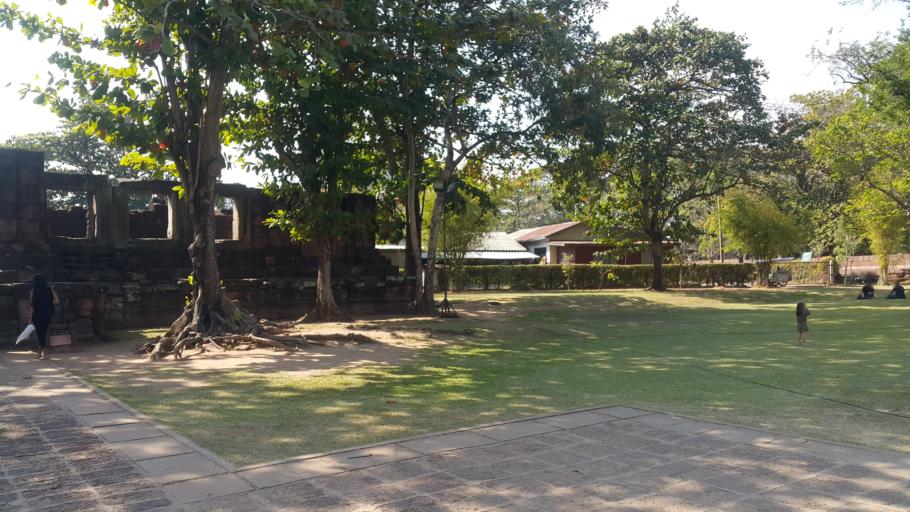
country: TH
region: Nakhon Ratchasima
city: Phimai
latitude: 15.2192
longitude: 102.4945
